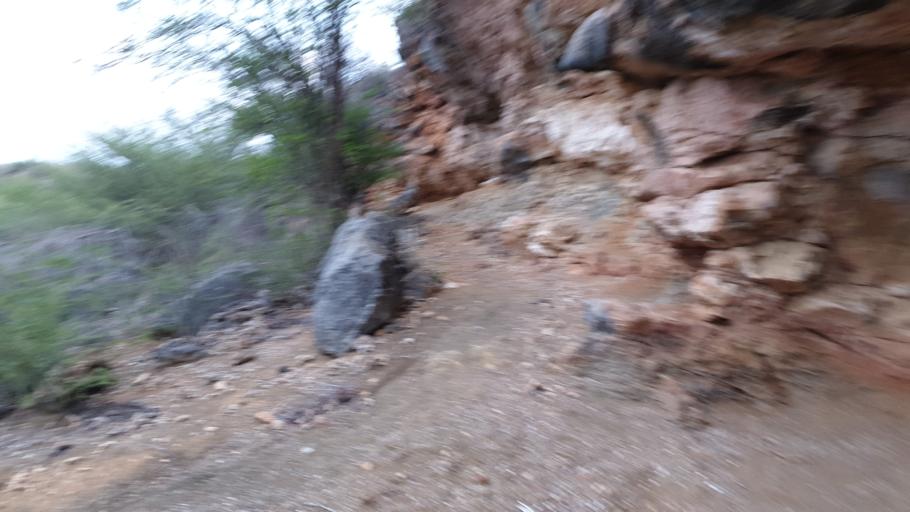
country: CW
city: Newport
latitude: 12.1277
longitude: -68.8143
